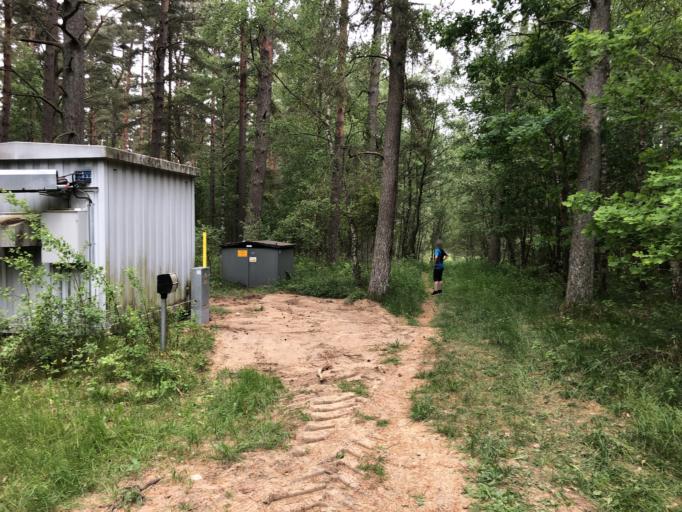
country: SE
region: Skane
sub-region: Lunds Kommun
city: Veberod
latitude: 55.6652
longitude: 13.5560
